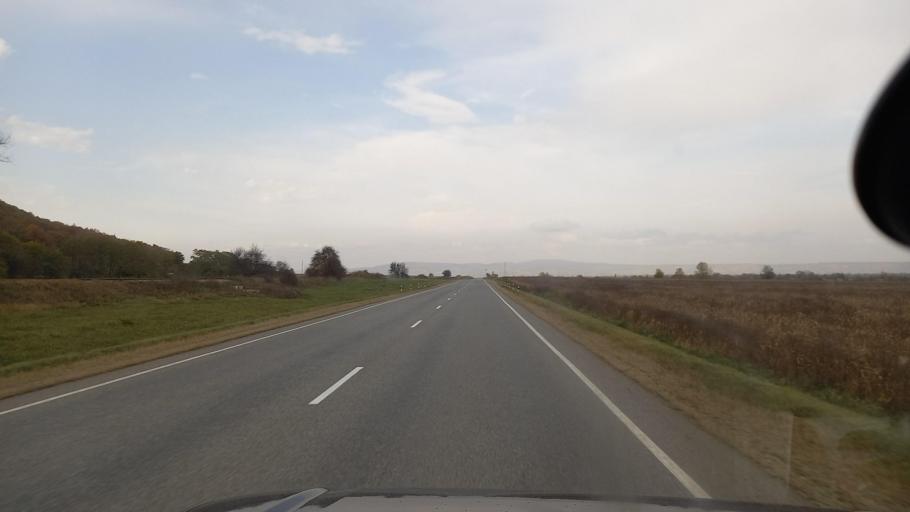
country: RU
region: Krasnodarskiy
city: Shedok
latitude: 44.2446
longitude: 40.8620
